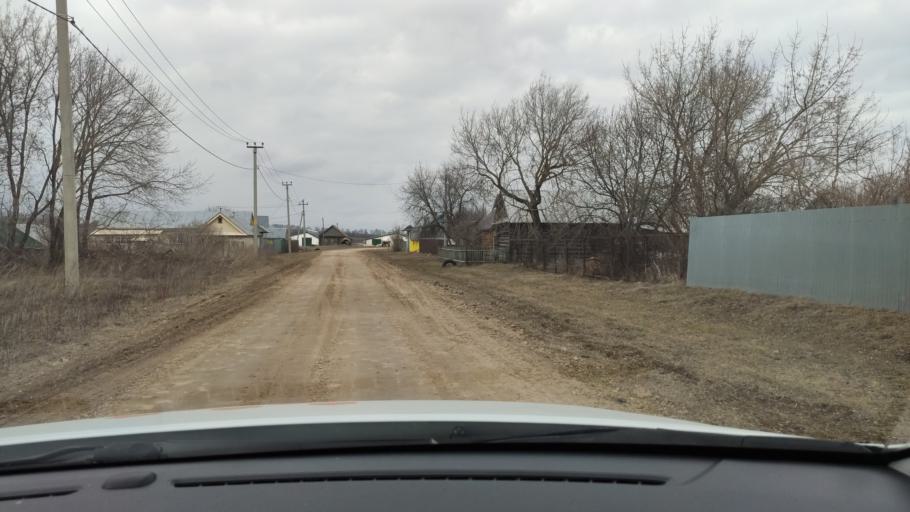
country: RU
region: Tatarstan
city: Vysokaya Gora
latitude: 56.2151
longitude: 49.3128
